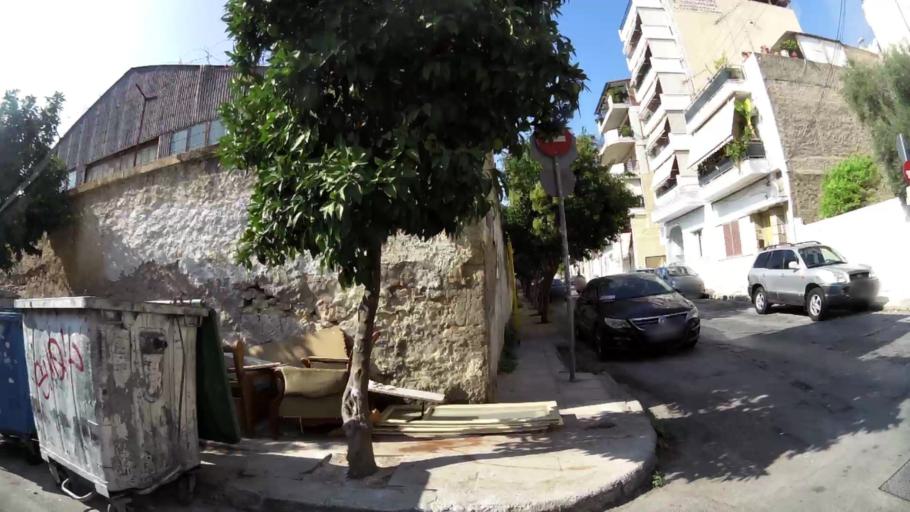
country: GR
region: Attica
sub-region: Nomos Piraios
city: Drapetsona
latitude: 37.9532
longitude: 23.6299
